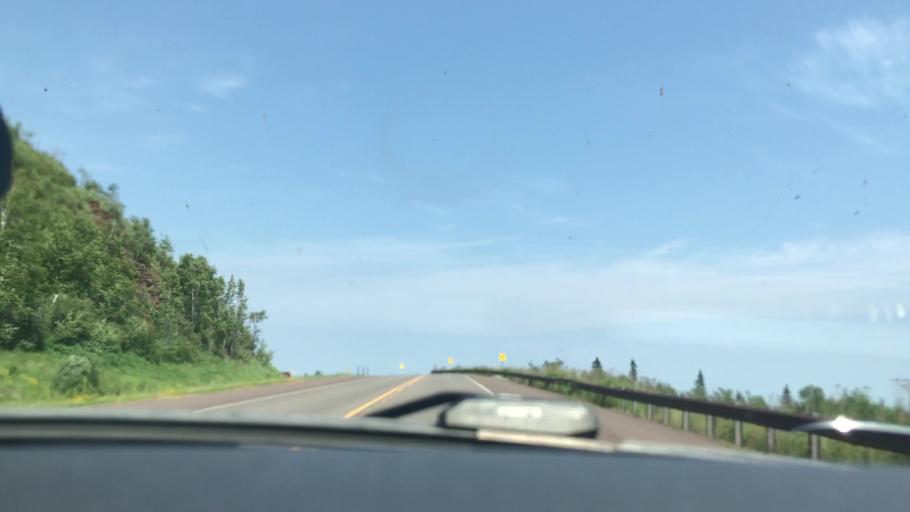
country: US
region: Minnesota
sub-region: Lake County
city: Silver Bay
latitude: 47.3040
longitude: -91.2462
